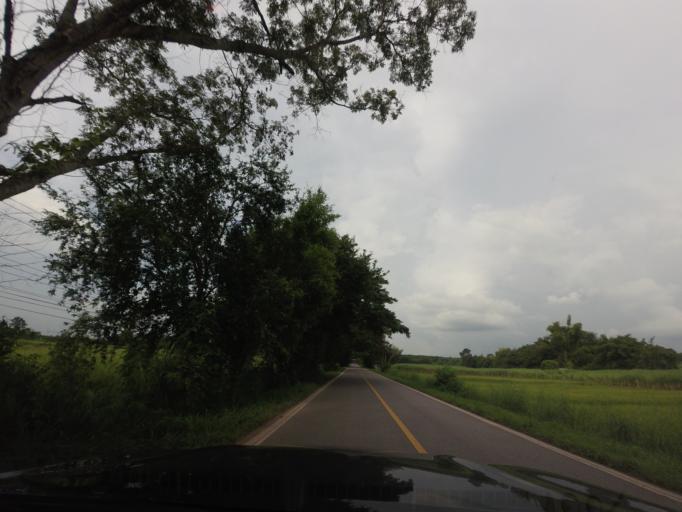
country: TH
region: Changwat Nong Bua Lamphu
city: Suwannakhuha
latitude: 17.5246
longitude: 102.3837
